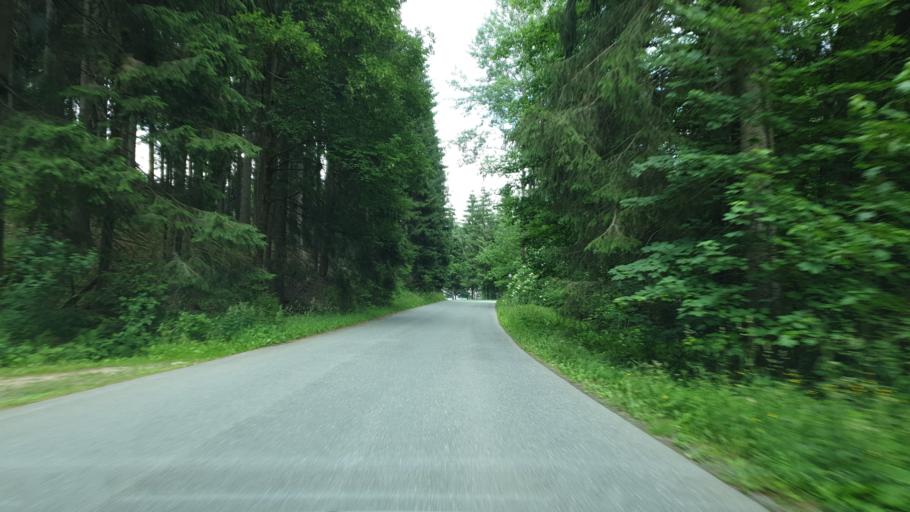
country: DE
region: Saxony
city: Tannenbergsthal
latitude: 50.4284
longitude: 12.4600
